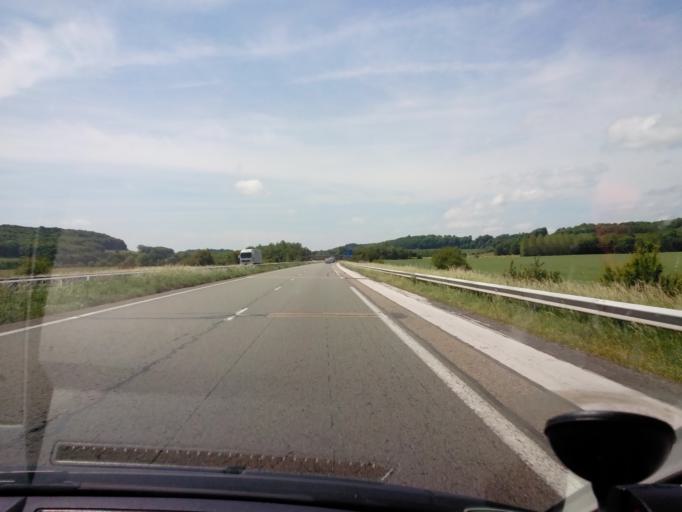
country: FR
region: Champagne-Ardenne
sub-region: Departement de la Haute-Marne
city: Avrecourt
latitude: 47.9841
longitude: 5.5059
